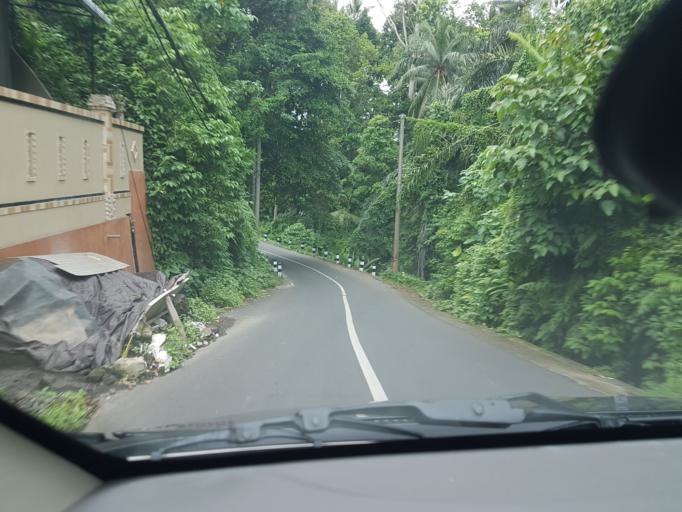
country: ID
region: Bali
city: Banjar Triwangsakeliki
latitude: -8.4574
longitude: 115.2759
